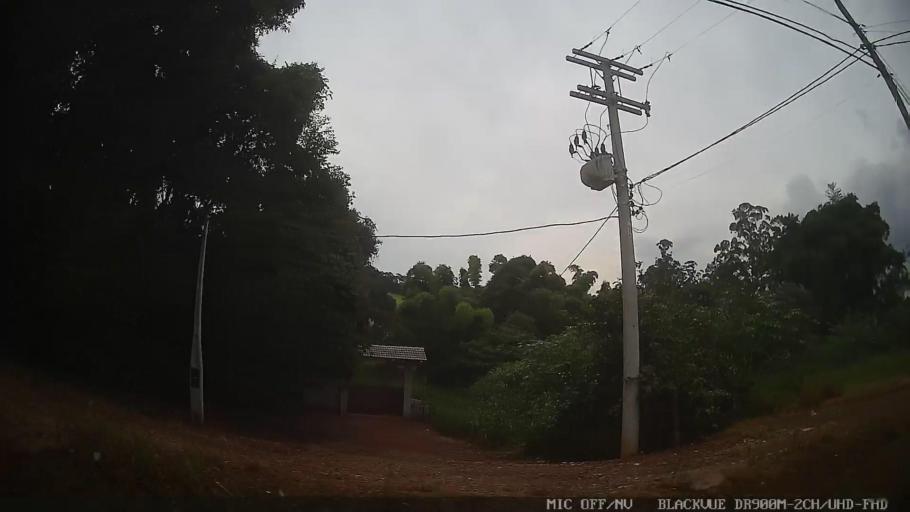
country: BR
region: Sao Paulo
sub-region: Atibaia
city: Atibaia
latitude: -23.1643
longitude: -46.6231
